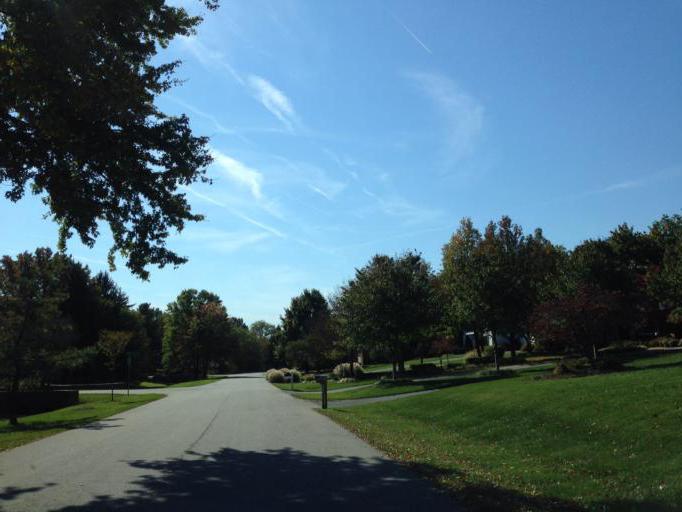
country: US
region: Maryland
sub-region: Howard County
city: Columbia
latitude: 39.2606
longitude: -76.8310
